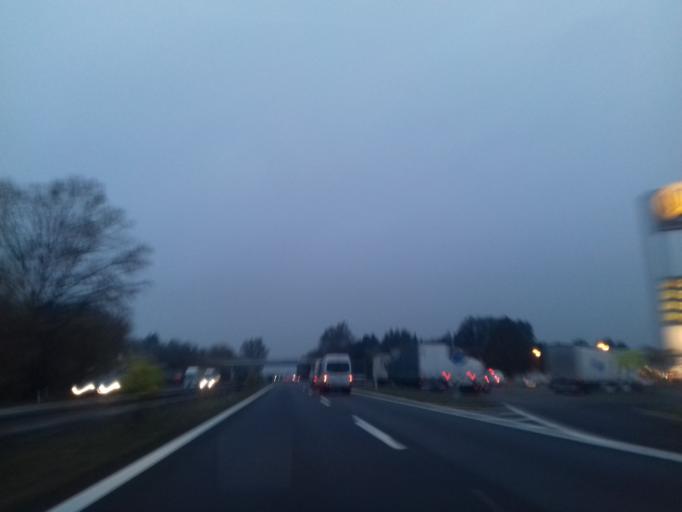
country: CZ
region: Olomoucky
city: Skrben
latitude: 49.6263
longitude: 17.1677
